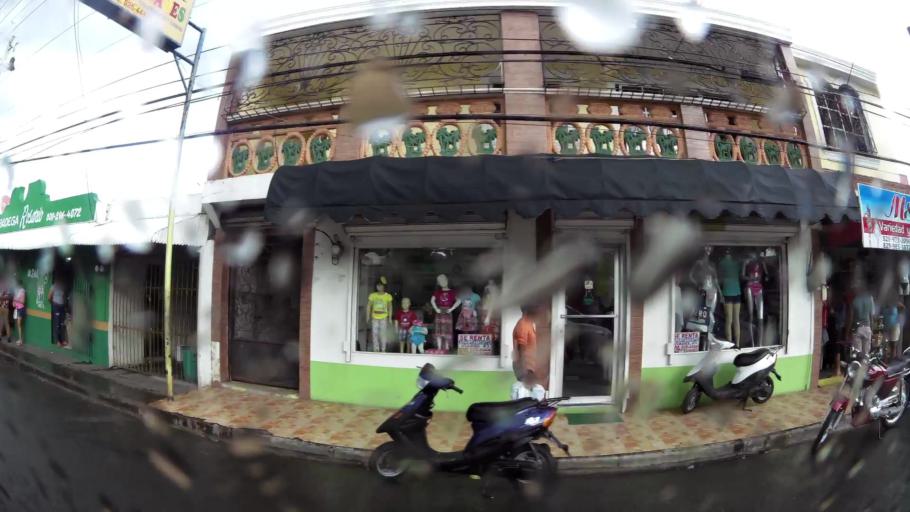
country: DO
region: Monsenor Nouel
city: Bonao
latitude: 18.9352
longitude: -70.4095
